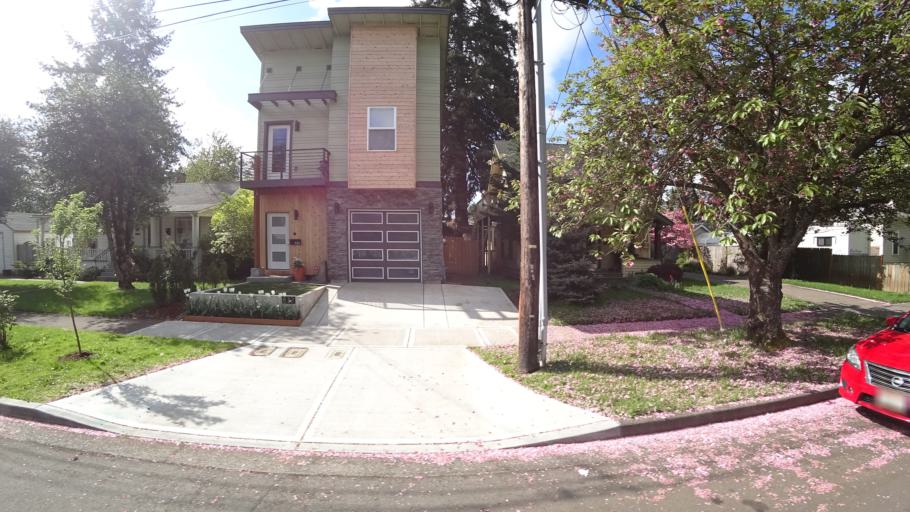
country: US
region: Oregon
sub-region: Washington County
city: Hillsboro
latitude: 45.5162
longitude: -122.9766
